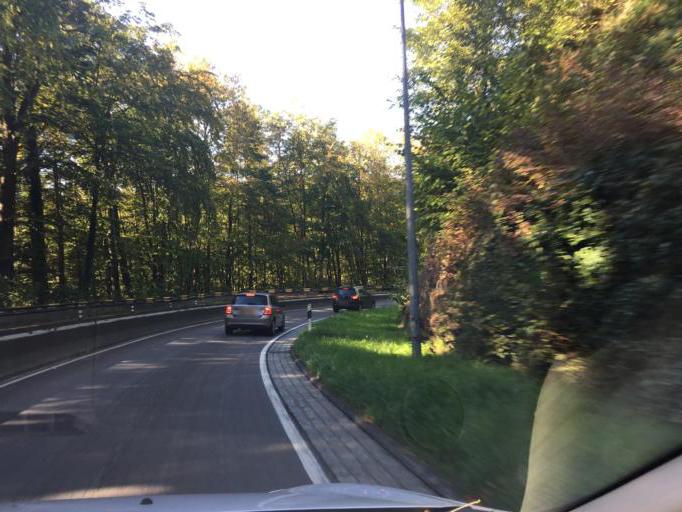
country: LU
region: Luxembourg
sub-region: Canton de Capellen
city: Kopstal
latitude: 49.6580
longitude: 6.0712
